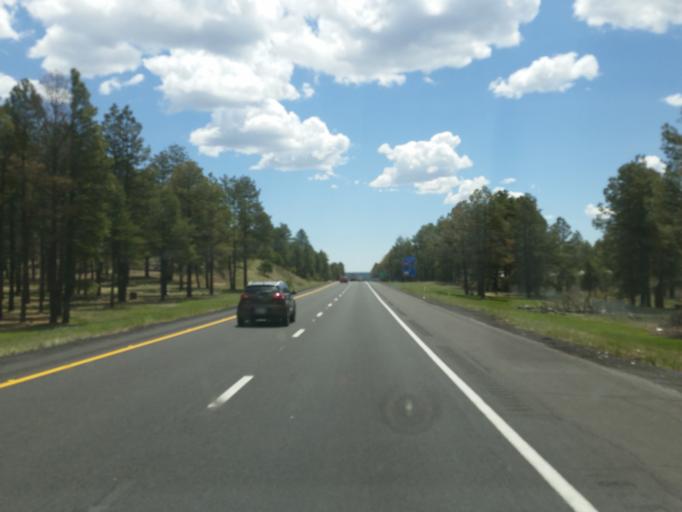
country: US
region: Arizona
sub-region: Coconino County
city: Flagstaff
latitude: 35.1805
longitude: -111.6921
